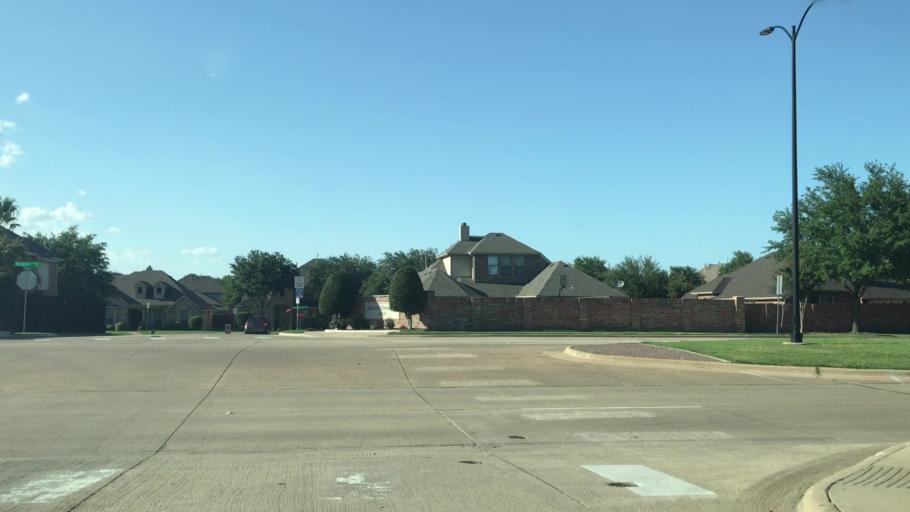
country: US
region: Texas
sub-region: Collin County
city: Frisco
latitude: 33.1379
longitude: -96.7767
